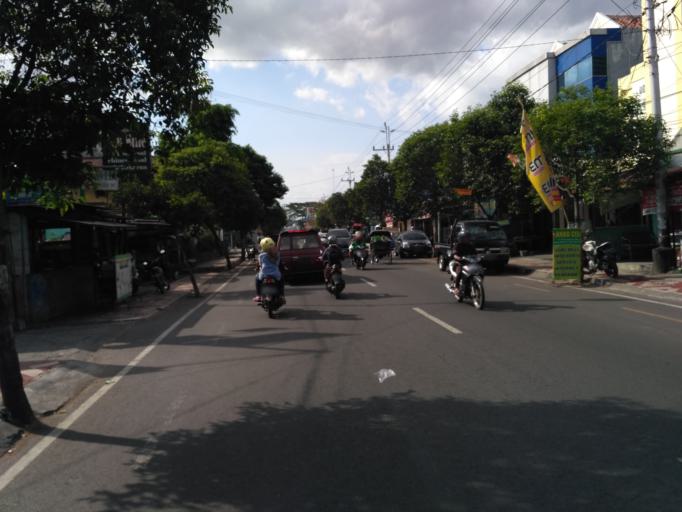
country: ID
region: Daerah Istimewa Yogyakarta
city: Yogyakarta
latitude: -7.8176
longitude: 110.3684
